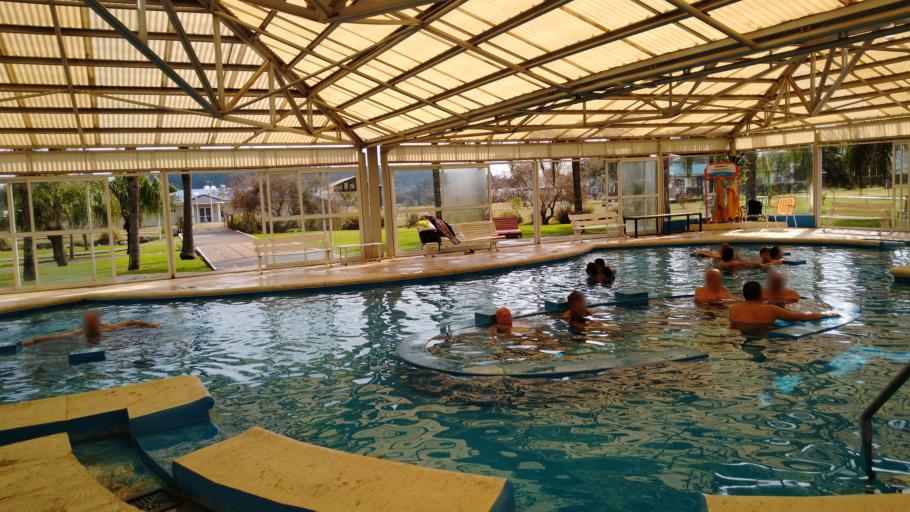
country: AR
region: Entre Rios
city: Chajari
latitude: -30.7450
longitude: -58.0133
